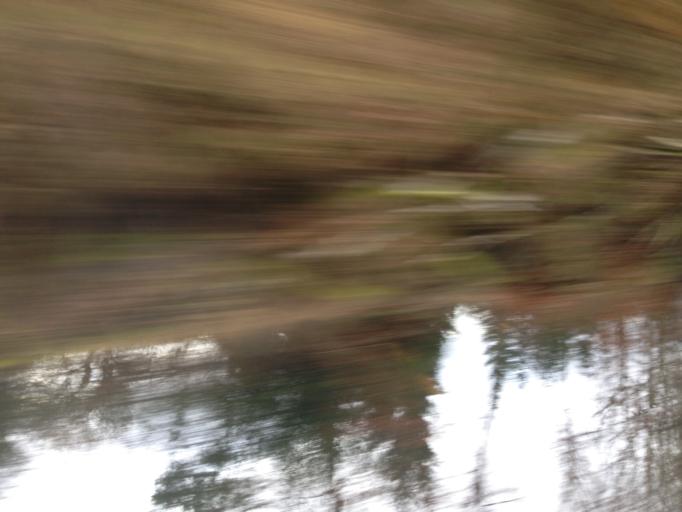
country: DE
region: Hesse
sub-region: Regierungsbezirk Giessen
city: Lich
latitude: 50.5190
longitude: 8.7785
